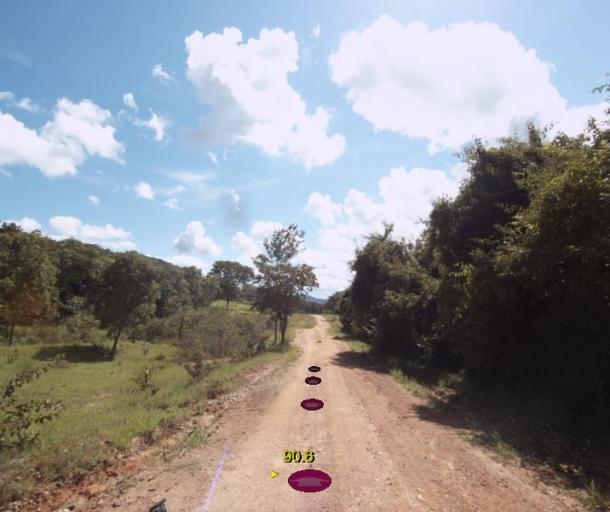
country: BR
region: Goias
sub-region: Pirenopolis
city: Pirenopolis
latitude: -15.7825
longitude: -48.9505
